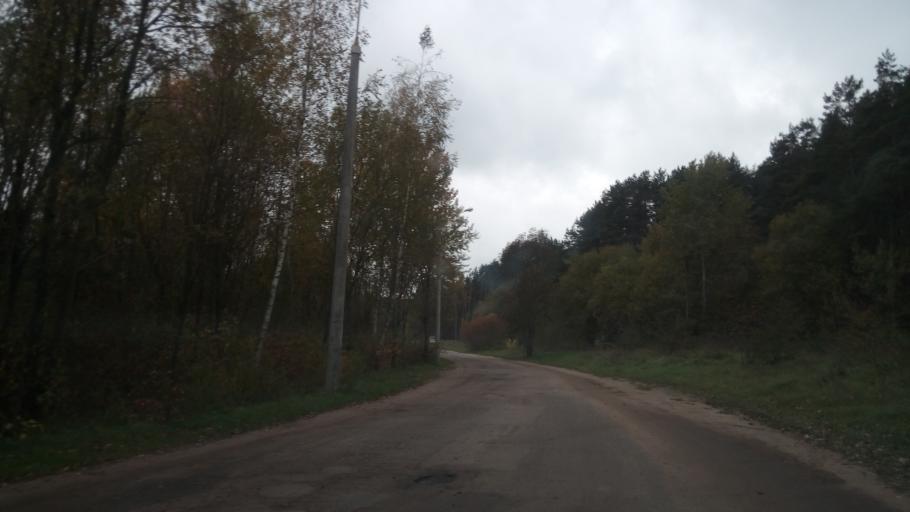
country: BY
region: Minsk
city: Zhdanovichy
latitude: 53.9600
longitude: 27.4438
